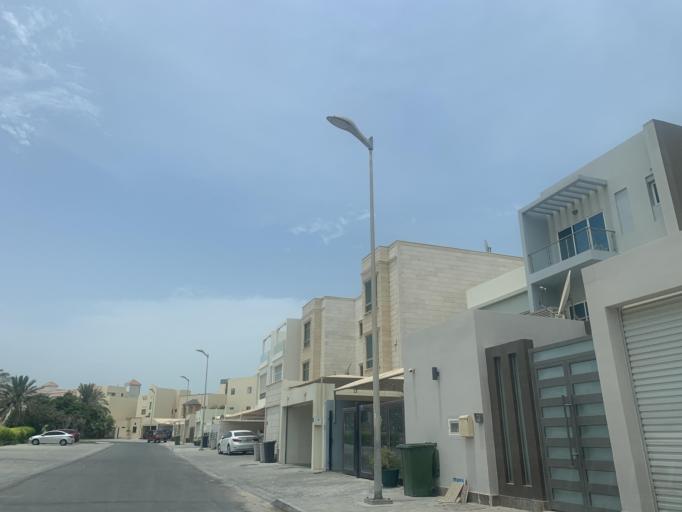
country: BH
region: Muharraq
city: Al Hadd
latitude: 26.2945
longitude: 50.6625
